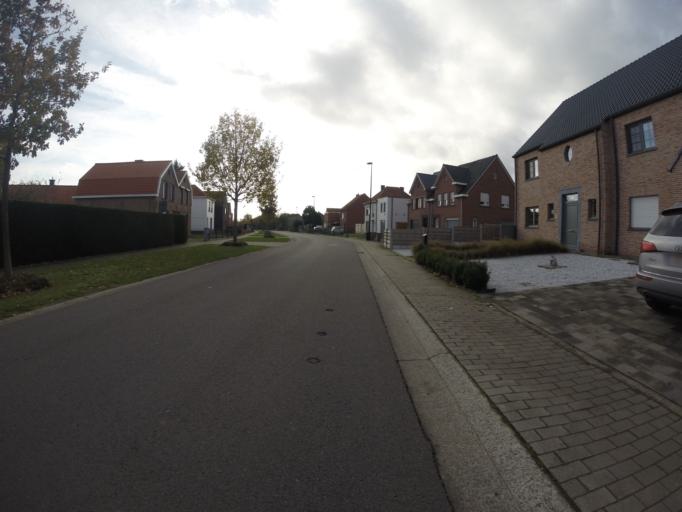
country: BE
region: Flanders
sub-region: Provincie Oost-Vlaanderen
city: Knesselare
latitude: 51.1343
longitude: 3.4158
